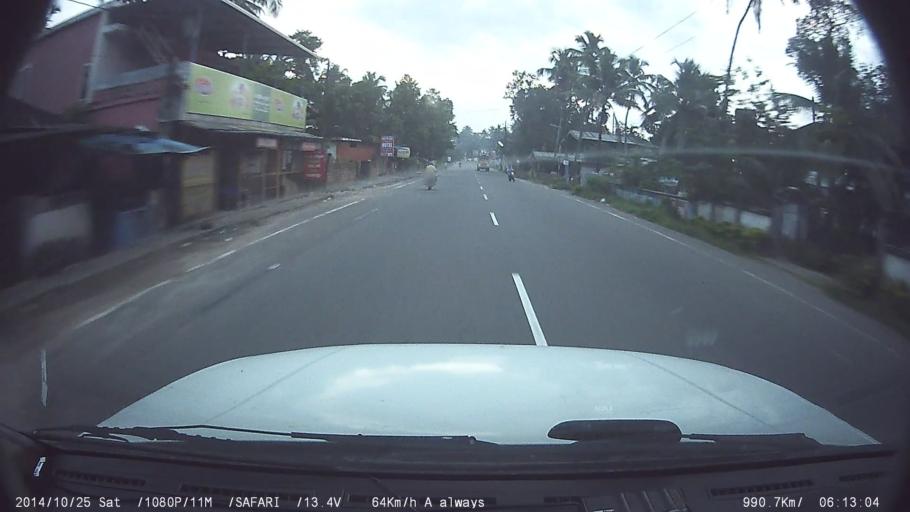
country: IN
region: Kerala
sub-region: Ernakulam
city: Perumpavur
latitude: 10.1468
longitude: 76.4587
